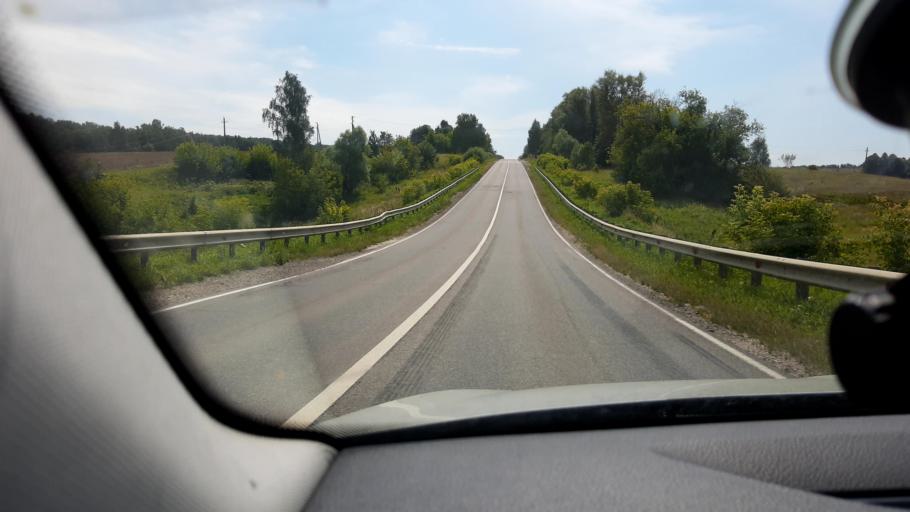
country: RU
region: Tula
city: Zaokskiy
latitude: 54.7797
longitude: 37.4347
